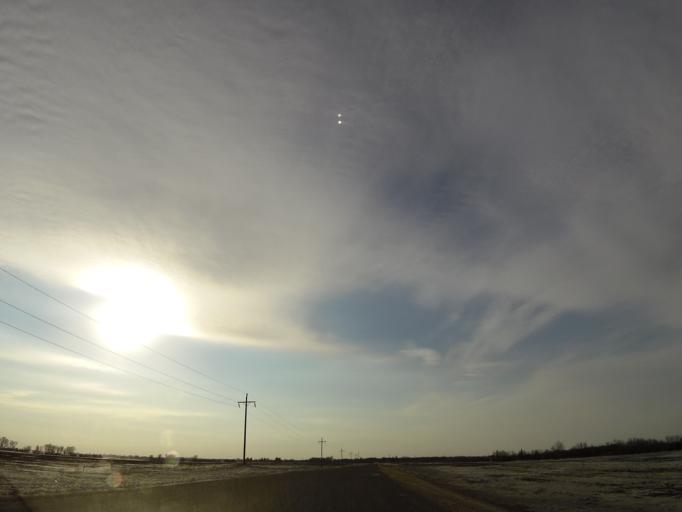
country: US
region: North Dakota
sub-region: Walsh County
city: Grafton
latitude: 48.4198
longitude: -97.3651
